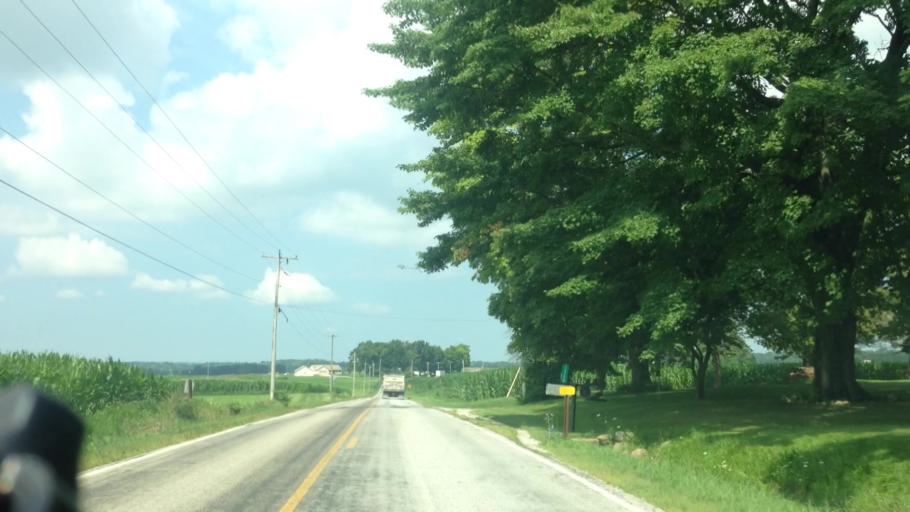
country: US
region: Ohio
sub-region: Wayne County
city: Dalton
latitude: 40.8632
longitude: -81.6705
